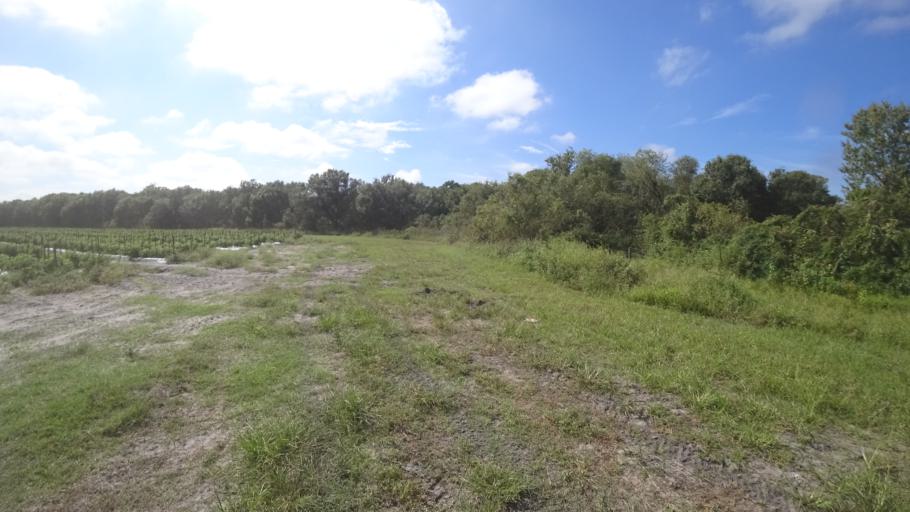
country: US
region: Florida
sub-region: DeSoto County
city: Nocatee
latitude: 27.2770
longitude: -82.0806
